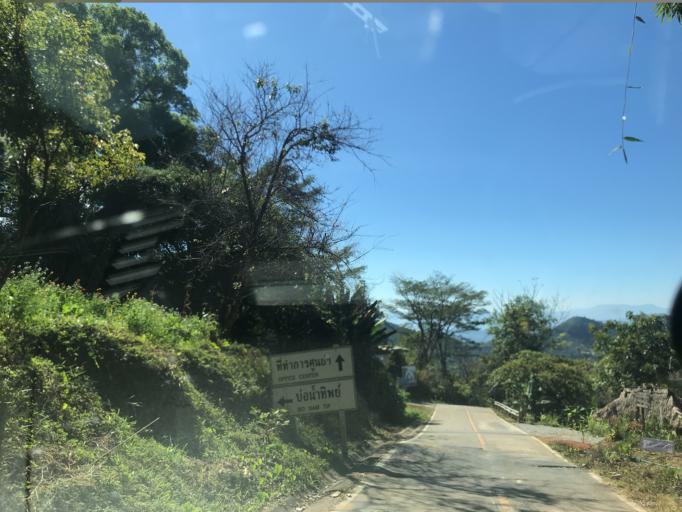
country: TH
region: Chiang Rai
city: Mae Lao
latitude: 19.8152
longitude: 99.5674
